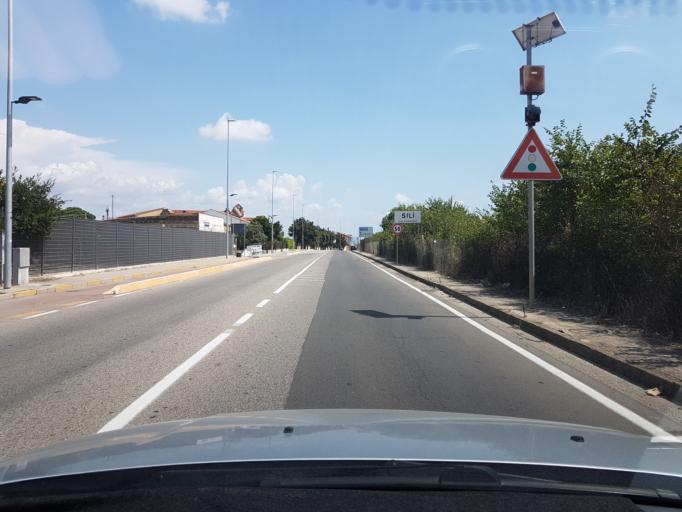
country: IT
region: Sardinia
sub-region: Provincia di Oristano
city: Sili
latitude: 39.9151
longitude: 8.6127
